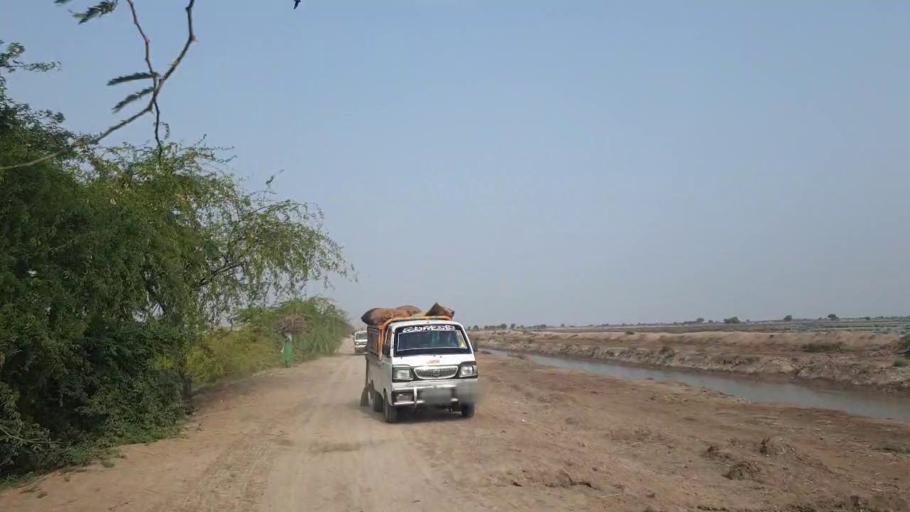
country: PK
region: Sindh
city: Badin
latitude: 24.7204
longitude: 68.7703
